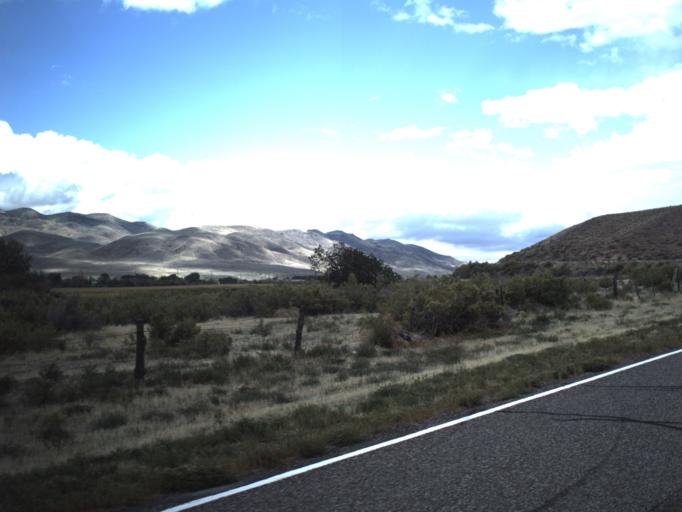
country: US
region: Utah
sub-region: Sevier County
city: Monroe
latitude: 38.6316
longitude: -112.1919
